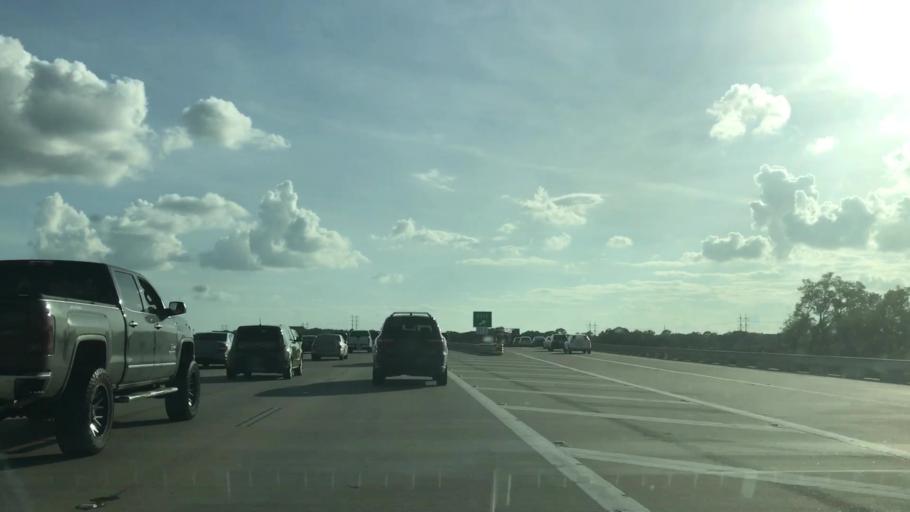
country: US
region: Texas
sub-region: Dallas County
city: Grand Prairie
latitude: 32.7816
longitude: -97.0236
